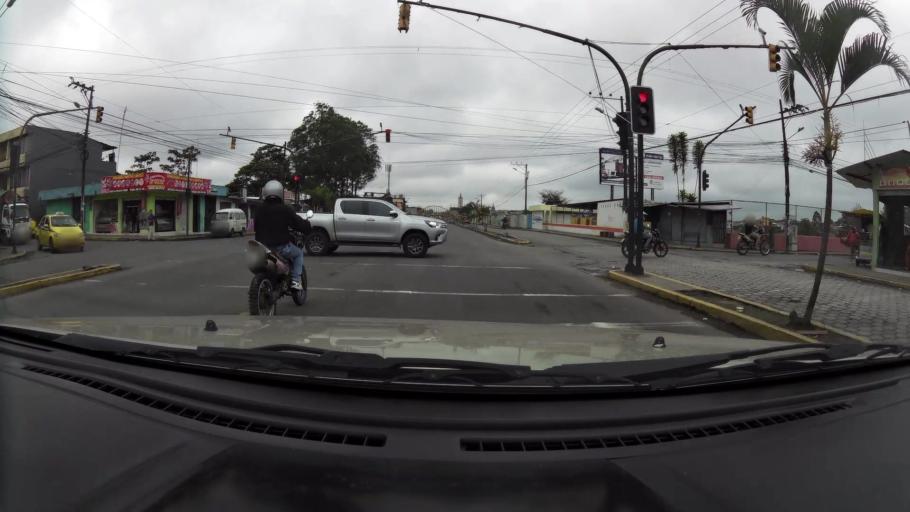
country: EC
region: Santo Domingo de los Tsachilas
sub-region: Canton Santo Domingo de los Colorados
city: Santo Domingo de los Colorados
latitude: -0.2445
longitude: -79.1838
